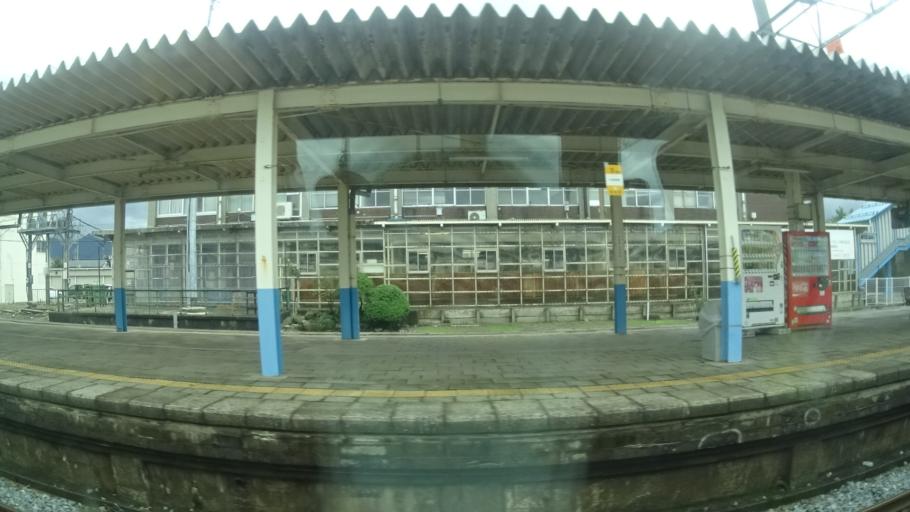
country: JP
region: Niigata
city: Murakami
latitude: 38.1205
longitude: 139.4468
